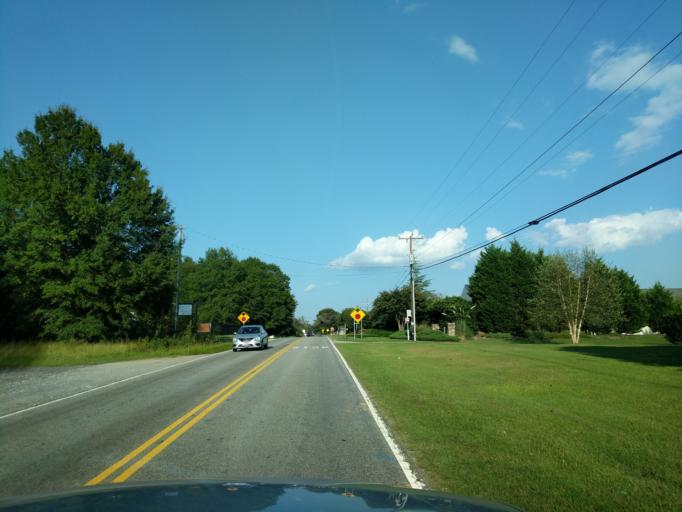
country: US
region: South Carolina
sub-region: Spartanburg County
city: Duncan
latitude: 34.8958
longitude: -82.1298
